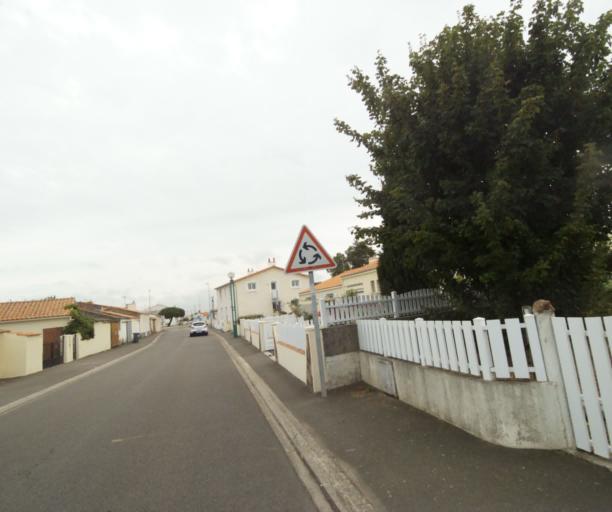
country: FR
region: Pays de la Loire
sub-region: Departement de la Vendee
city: Chateau-d'Olonne
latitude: 46.4986
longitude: -1.7569
